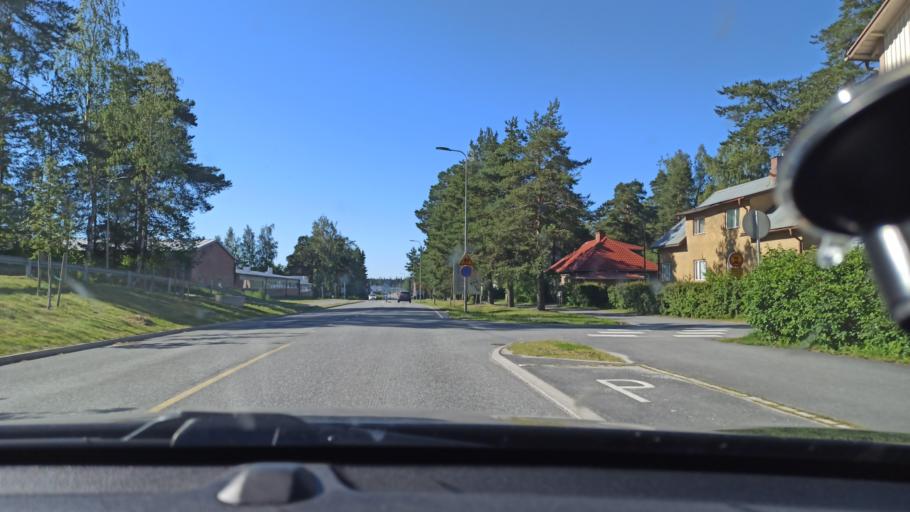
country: FI
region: Ostrobothnia
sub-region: Jakobstadsregionen
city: Jakobstad
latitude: 63.6828
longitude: 22.7142
